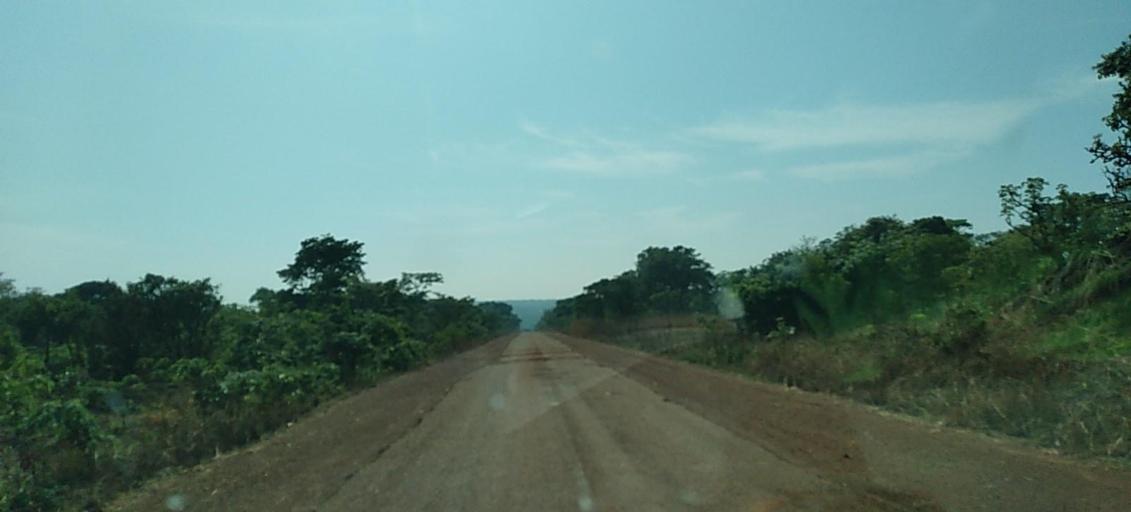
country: ZM
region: North-Western
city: Mwinilunga
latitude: -11.8225
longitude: 25.1096
